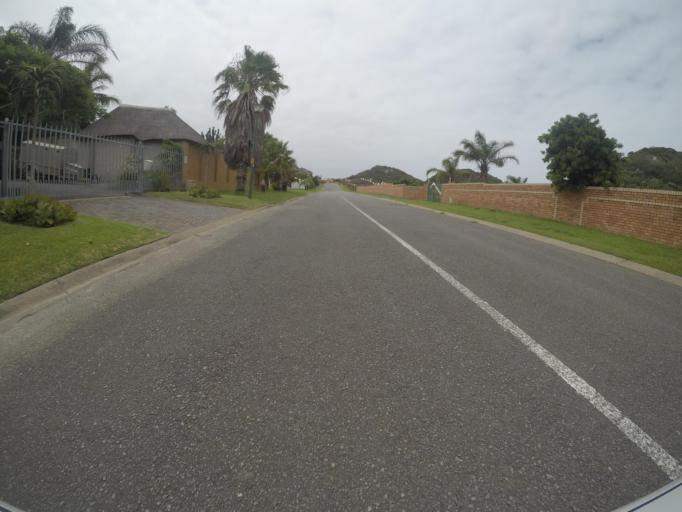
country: ZA
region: Eastern Cape
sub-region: Buffalo City Metropolitan Municipality
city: East London
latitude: -32.9806
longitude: 27.9535
